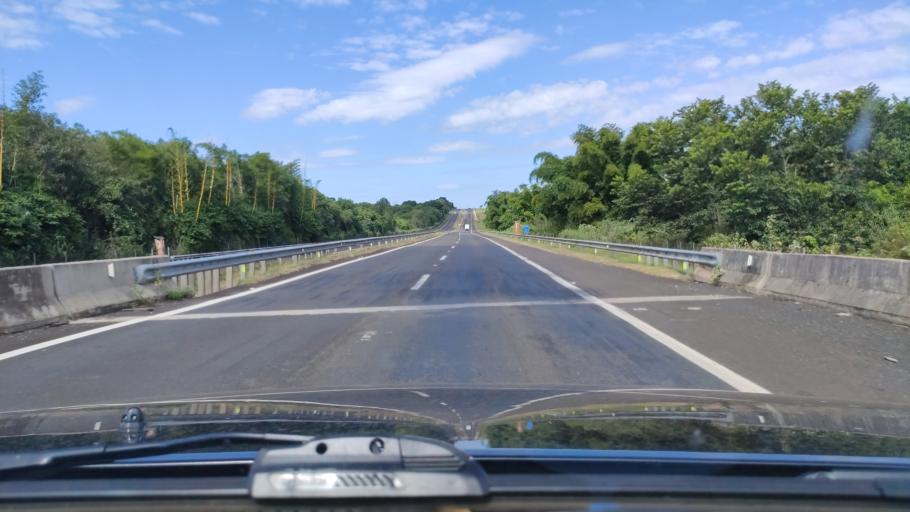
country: BR
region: Sao Paulo
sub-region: Rancharia
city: Rancharia
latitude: -22.4886
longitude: -50.9170
